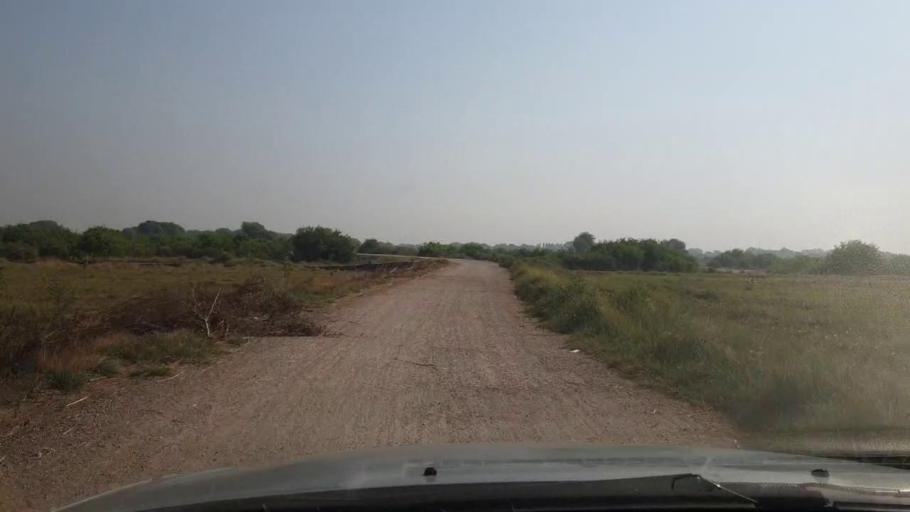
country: PK
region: Sindh
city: Tando Jam
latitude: 25.2792
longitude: 68.5311
